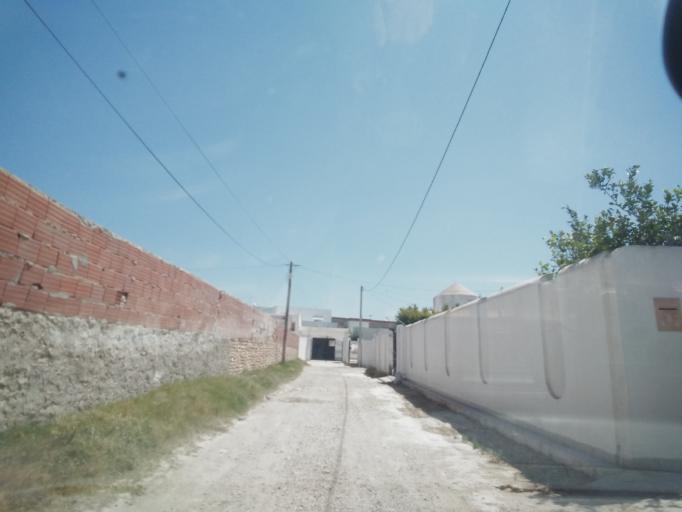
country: TN
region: Safaqis
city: Al Qarmadah
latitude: 34.8233
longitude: 10.7642
